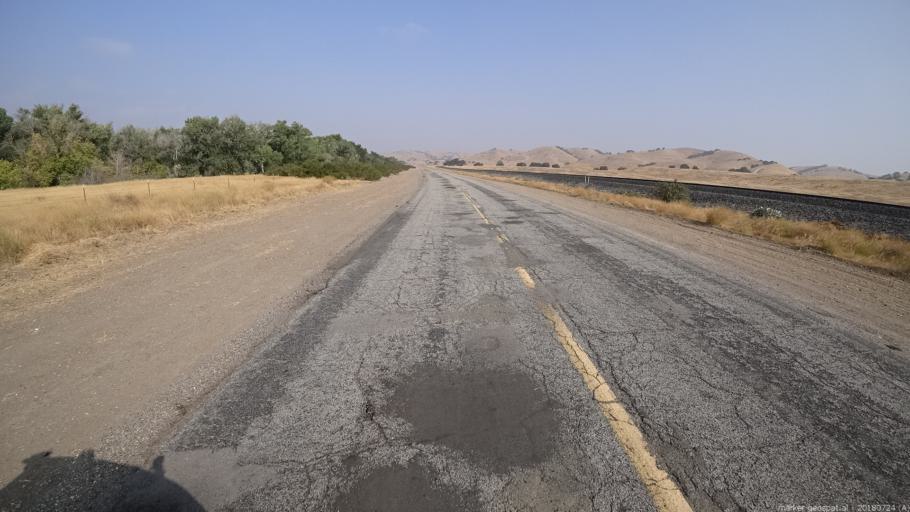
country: US
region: California
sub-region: San Luis Obispo County
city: San Miguel
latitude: 35.8480
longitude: -120.7542
